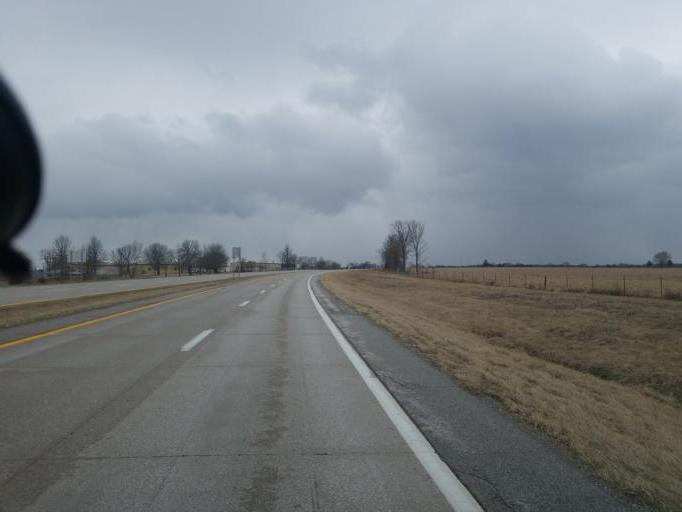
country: US
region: Missouri
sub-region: Macon County
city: Macon
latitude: 39.8000
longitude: -92.4750
